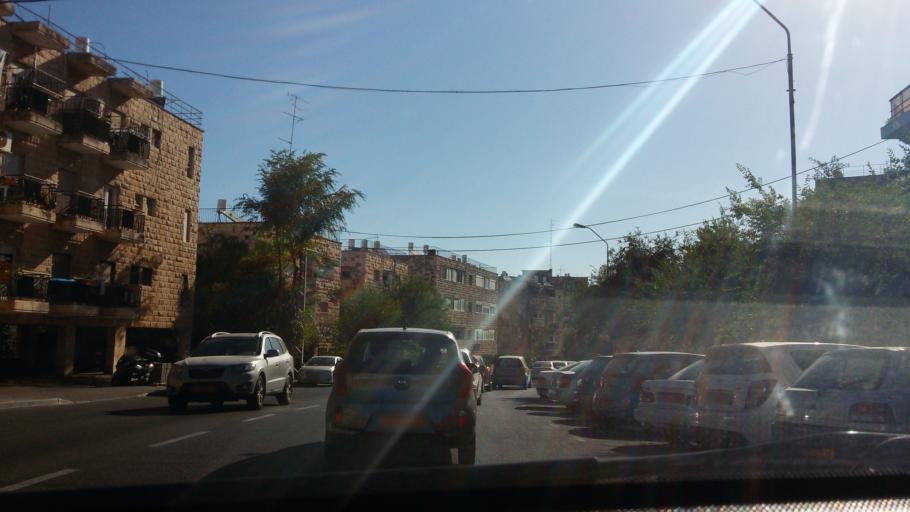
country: IL
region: Jerusalem
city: Jerusalem
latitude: 31.7680
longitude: 35.2064
